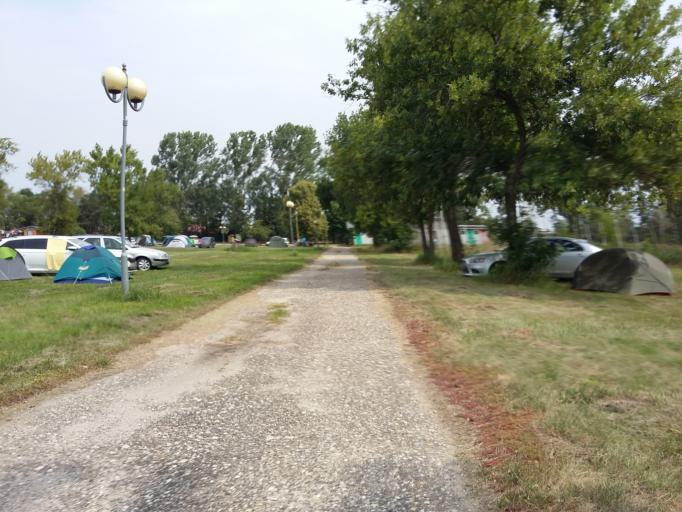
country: AT
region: Lower Austria
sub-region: Politischer Bezirk Ganserndorf
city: Drosing
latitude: 48.4897
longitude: 16.9562
